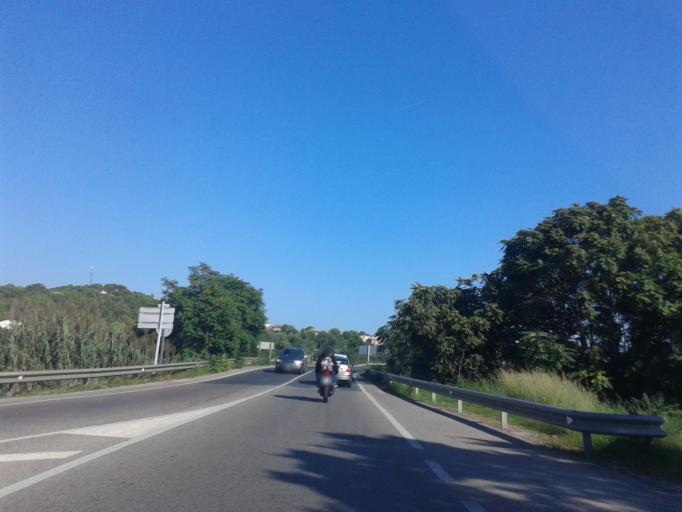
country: ES
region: Catalonia
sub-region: Provincia de Tarragona
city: Calafell
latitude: 41.1929
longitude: 1.5730
